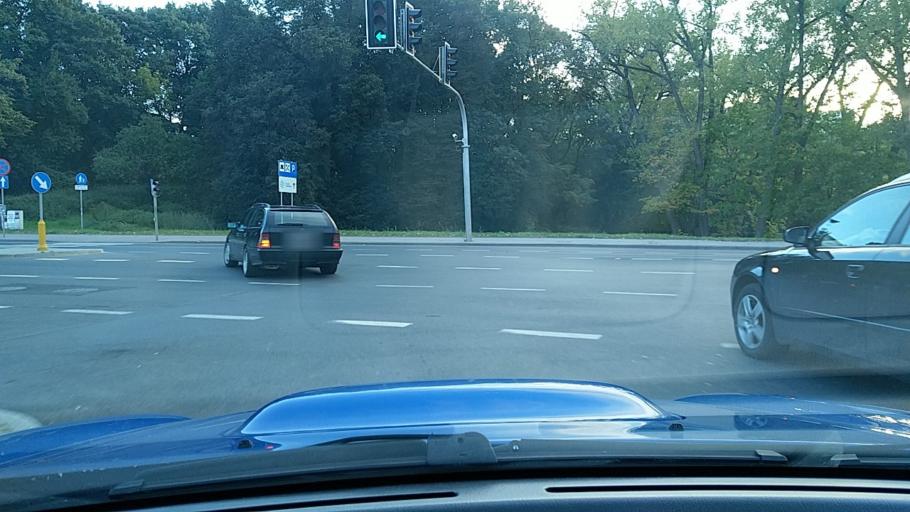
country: PL
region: Warmian-Masurian Voivodeship
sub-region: Powiat olsztynski
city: Olsztyn
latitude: 53.7694
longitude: 20.4821
